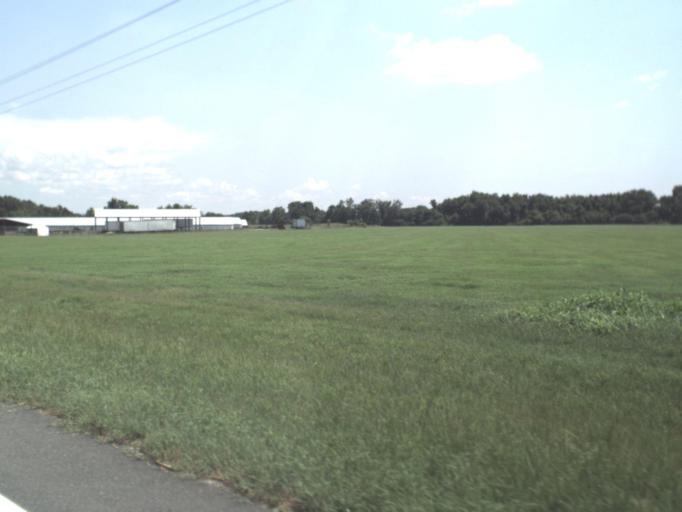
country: US
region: Florida
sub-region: Lafayette County
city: Mayo
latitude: 30.0993
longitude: -83.2391
